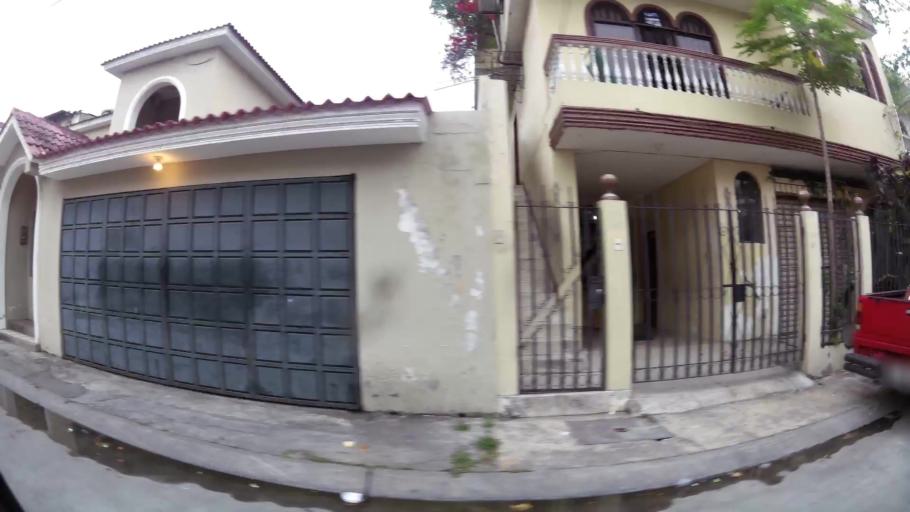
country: EC
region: Guayas
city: Eloy Alfaro
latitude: -2.1421
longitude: -79.9053
